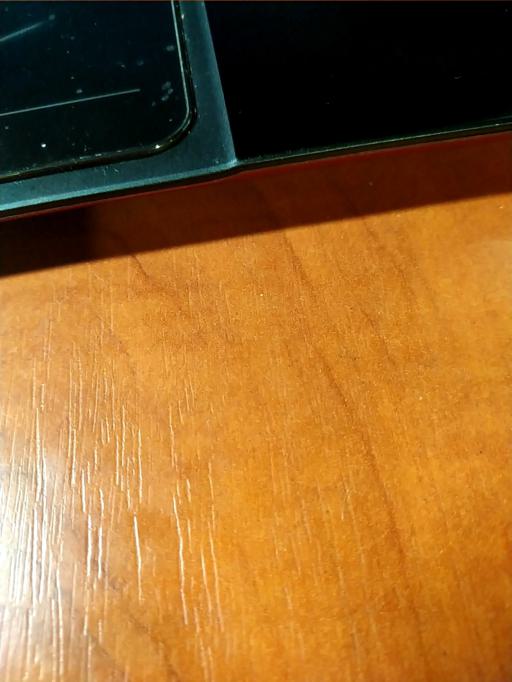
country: RU
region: Tverskaya
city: Zubtsov
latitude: 56.3269
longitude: 34.6754
